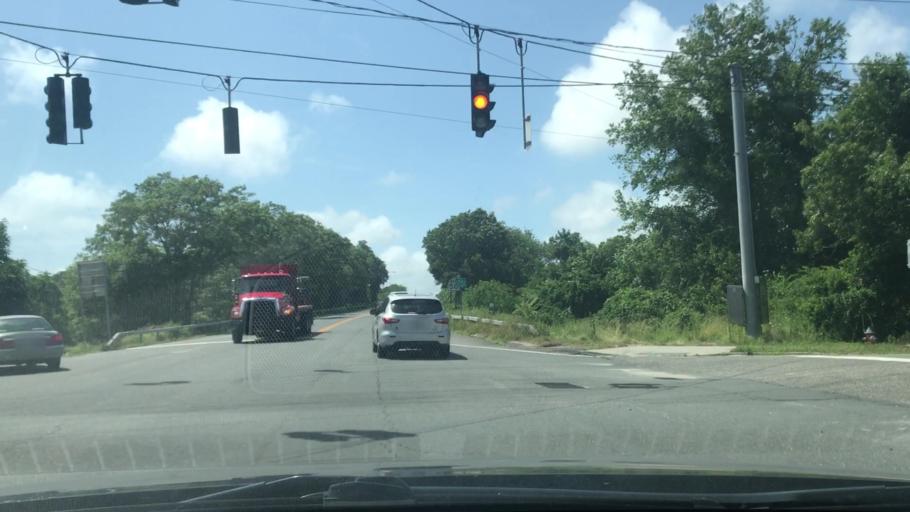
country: US
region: New York
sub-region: Suffolk County
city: Calverton
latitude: 40.9159
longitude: -72.7066
